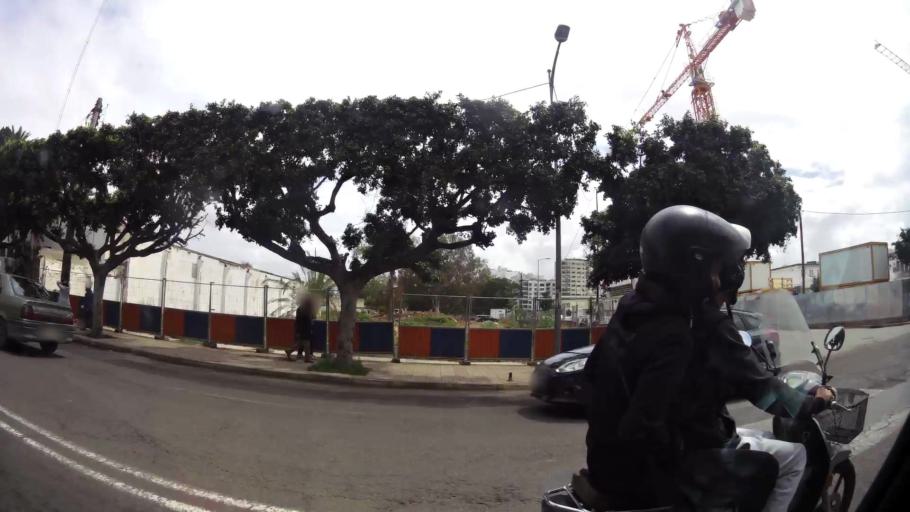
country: MA
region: Grand Casablanca
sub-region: Casablanca
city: Casablanca
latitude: 33.5871
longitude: -7.6282
